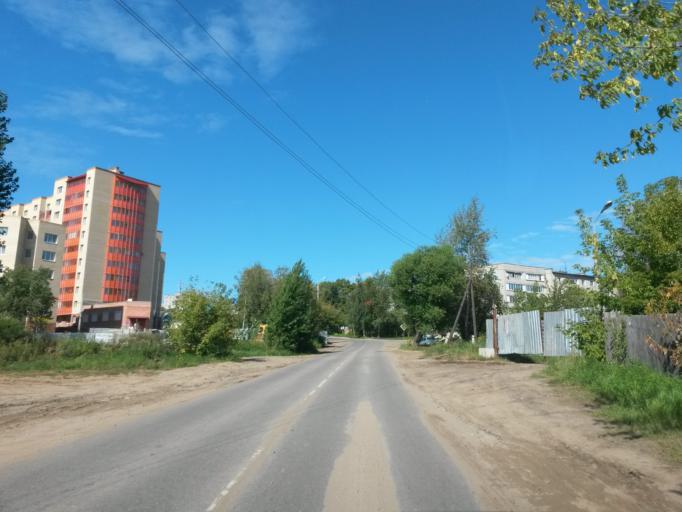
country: RU
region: Jaroslavl
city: Yaroslavl
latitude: 57.5773
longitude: 39.8668
